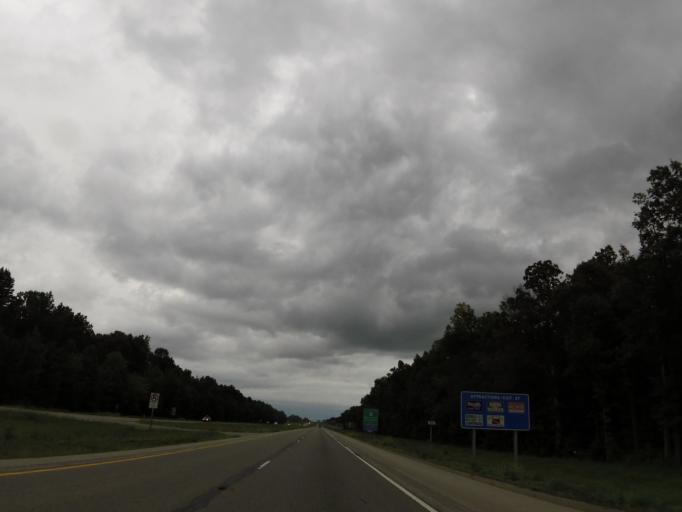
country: US
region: Illinois
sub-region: Massac County
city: Metropolis
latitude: 37.1503
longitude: -88.6825
